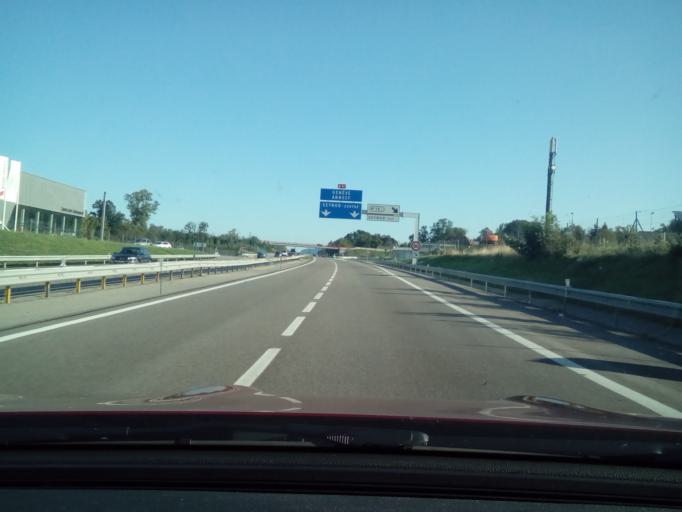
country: FR
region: Rhone-Alpes
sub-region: Departement de la Haute-Savoie
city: Viuz-la-Chiesaz
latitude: 45.8449
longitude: 6.0570
